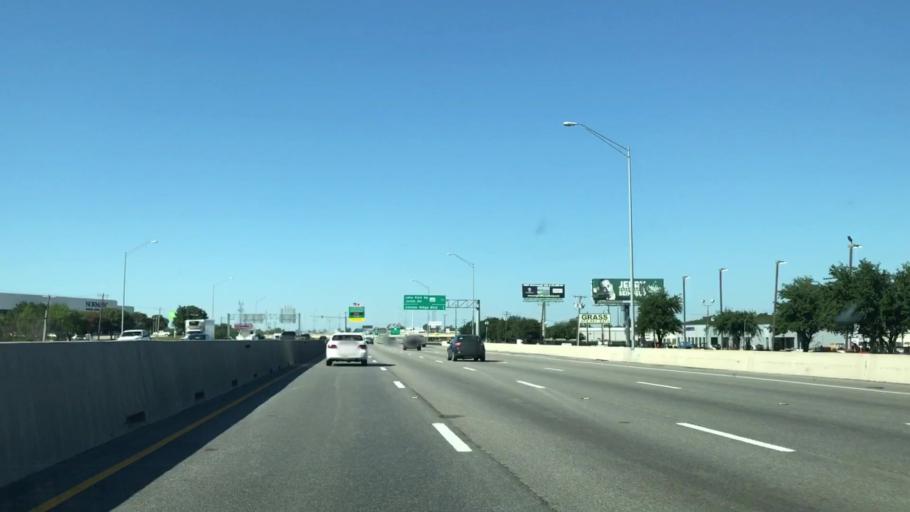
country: US
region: Texas
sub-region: Denton County
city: Lewisville
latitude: 33.0570
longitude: -97.0118
